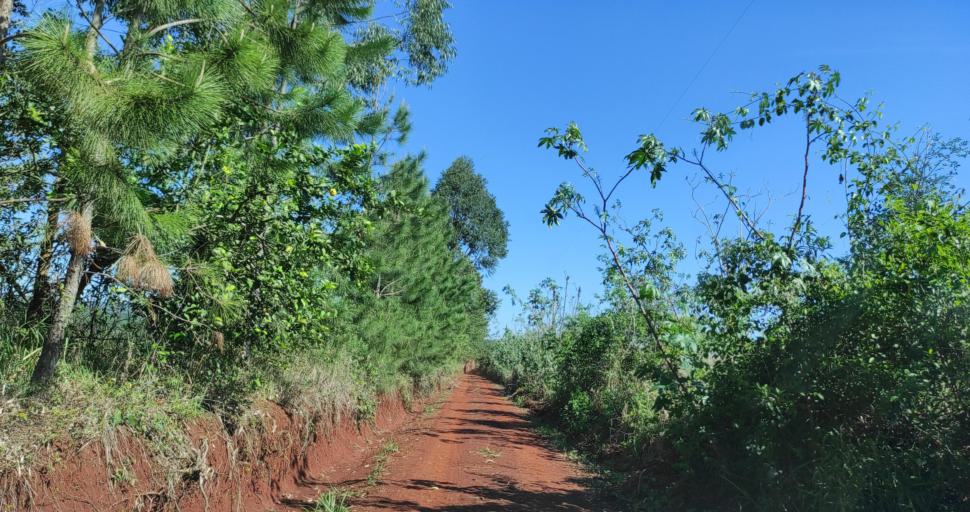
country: AR
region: Misiones
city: Capiovi
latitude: -26.9122
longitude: -55.0198
